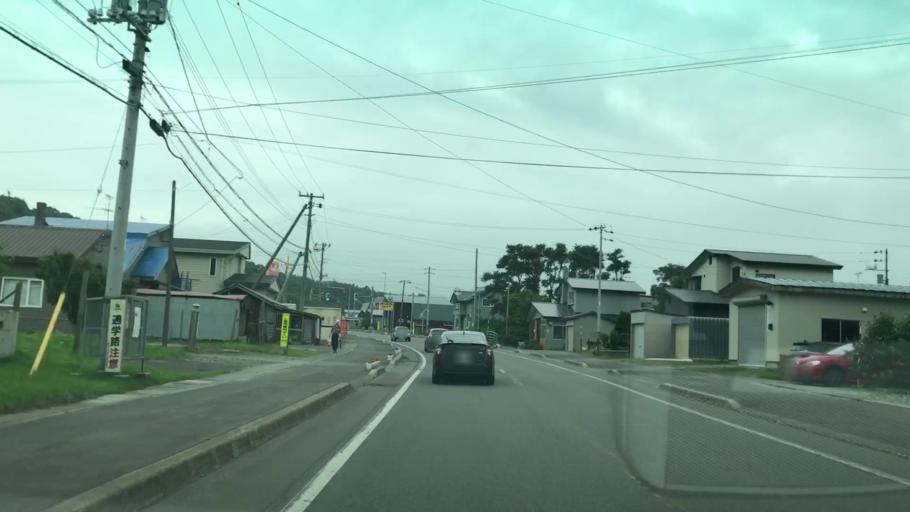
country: JP
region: Hokkaido
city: Iwanai
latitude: 42.7760
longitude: 140.3053
